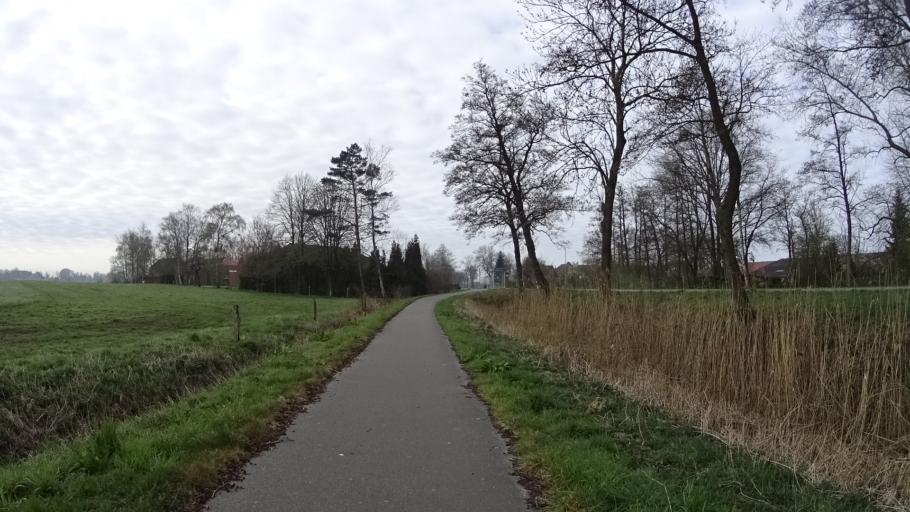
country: DE
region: Lower Saxony
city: Upgant-Schott
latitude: 53.4321
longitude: 7.3201
